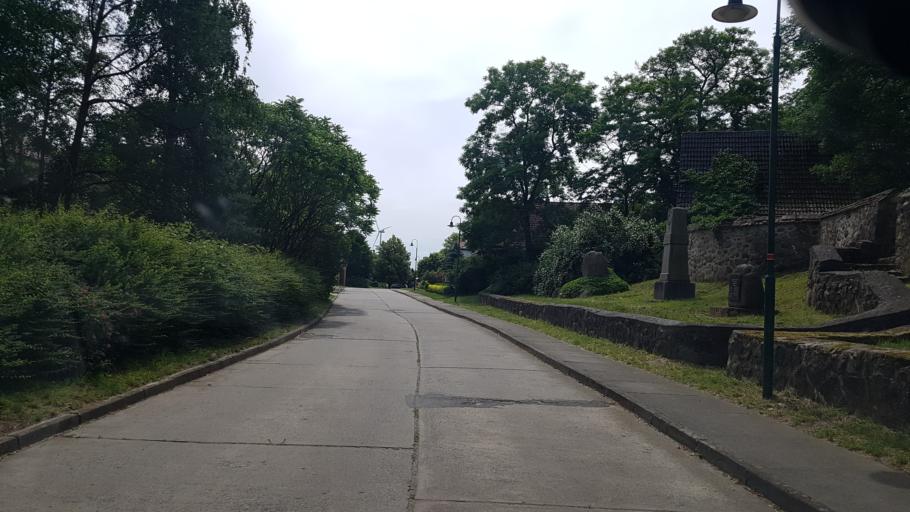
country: DE
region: Mecklenburg-Vorpommern
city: Strasburg
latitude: 53.4498
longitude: 13.8056
